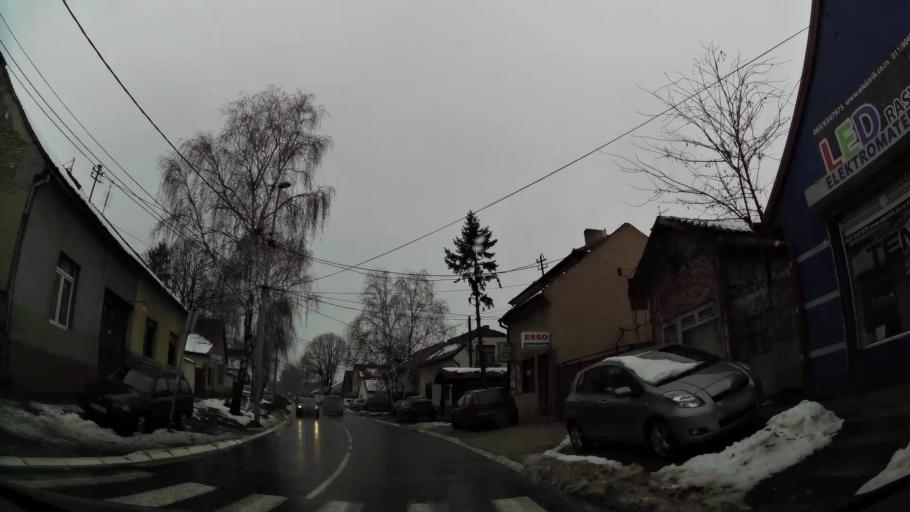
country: RS
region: Central Serbia
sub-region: Belgrade
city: Zemun
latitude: 44.8452
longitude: 20.4026
